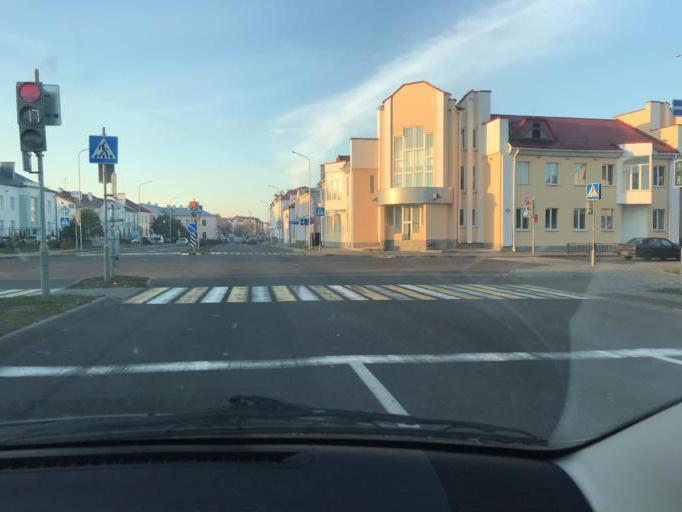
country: BY
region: Brest
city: Pinsk
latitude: 52.1136
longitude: 26.1041
